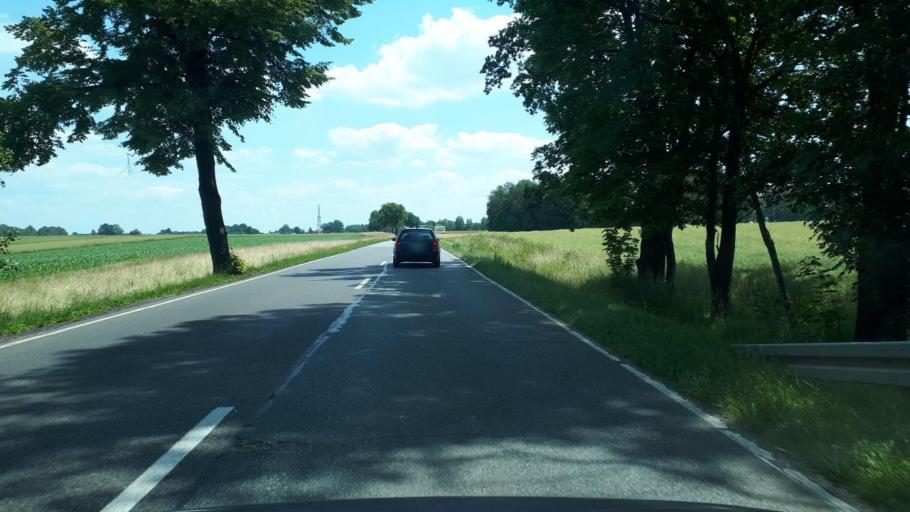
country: PL
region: Silesian Voivodeship
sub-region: Powiat pszczynski
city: Miedzna
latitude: 49.9696
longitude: 19.0352
